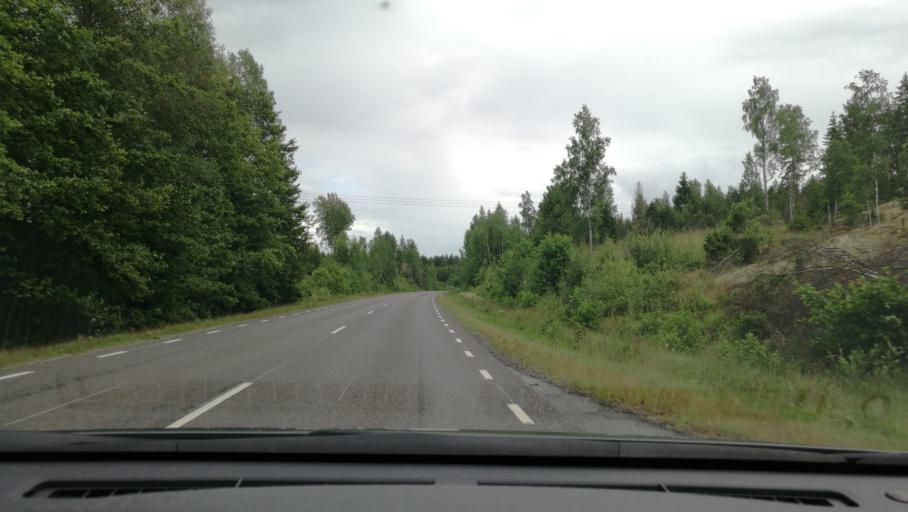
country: SE
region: OEstergoetland
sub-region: Norrkopings Kommun
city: Svartinge
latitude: 58.7873
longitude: 15.9630
